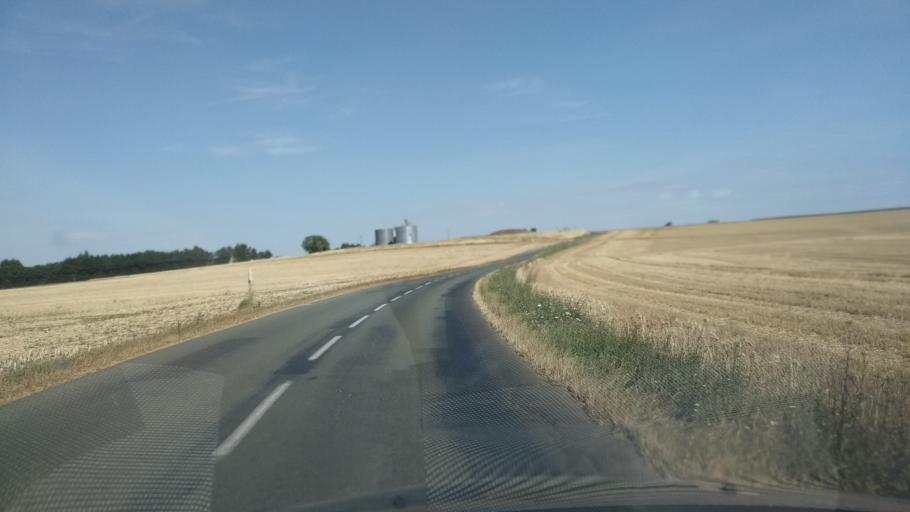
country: FR
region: Poitou-Charentes
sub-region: Departement de la Vienne
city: Vouille
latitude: 46.6846
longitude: 0.1626
